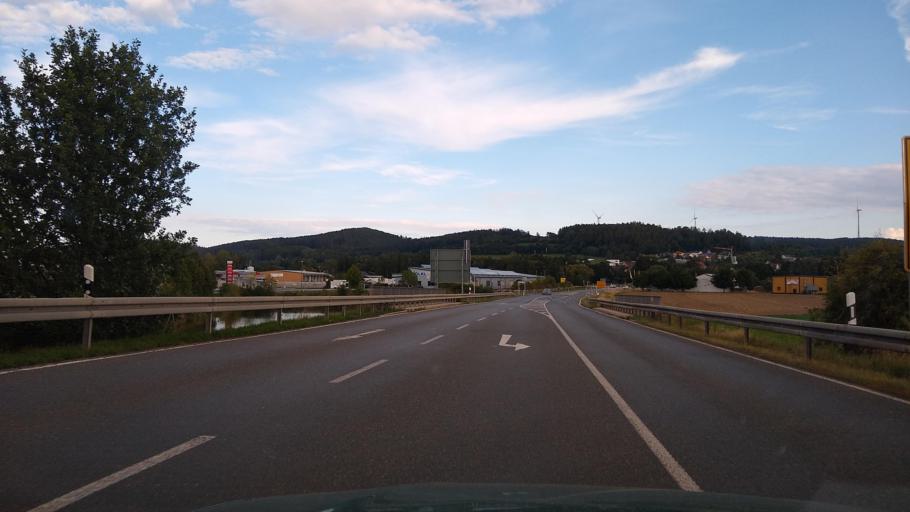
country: DE
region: Bavaria
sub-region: Upper Palatinate
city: Luhe-Wildenau
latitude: 49.5912
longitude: 12.1444
